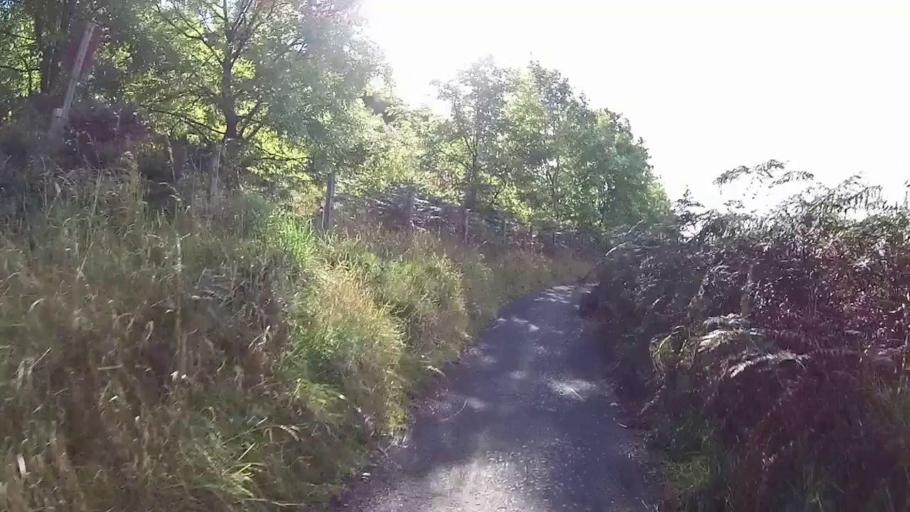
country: GB
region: Scotland
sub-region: Fife
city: Ballingry
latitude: 56.1790
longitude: -3.3481
